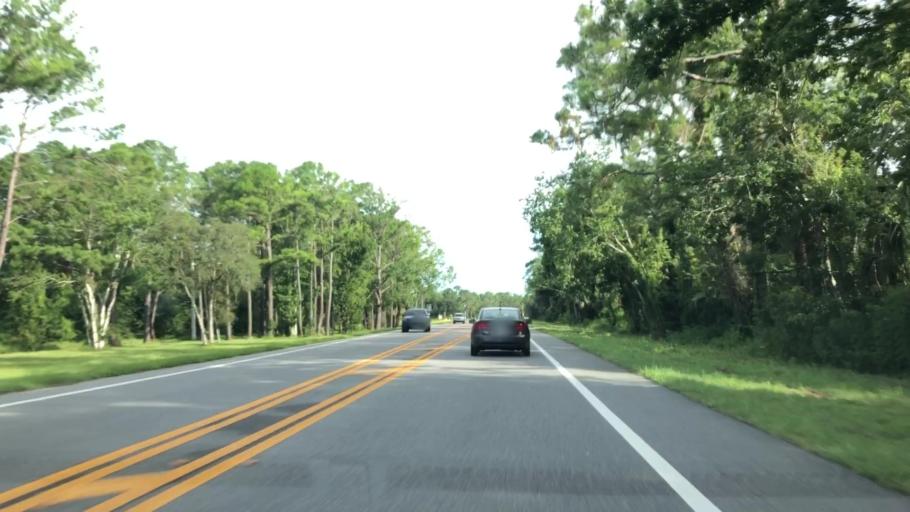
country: US
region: Florida
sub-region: Saint Johns County
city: Palm Valley
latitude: 30.1770
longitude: -81.3763
